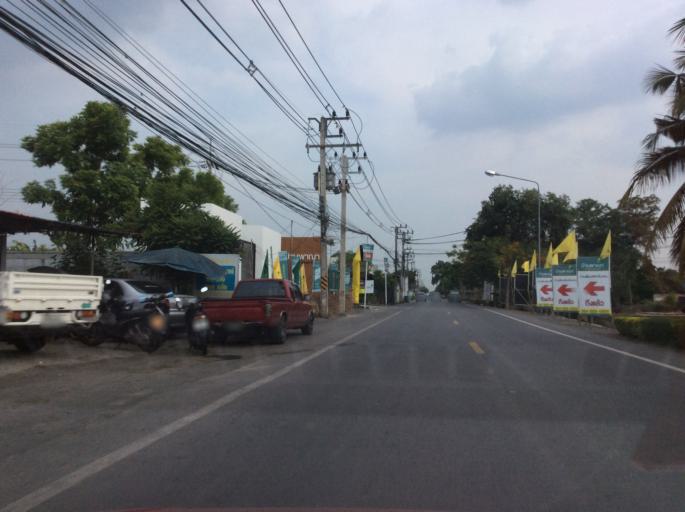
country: TH
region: Pathum Thani
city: Lam Luk Ka
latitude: 13.9620
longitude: 100.7277
